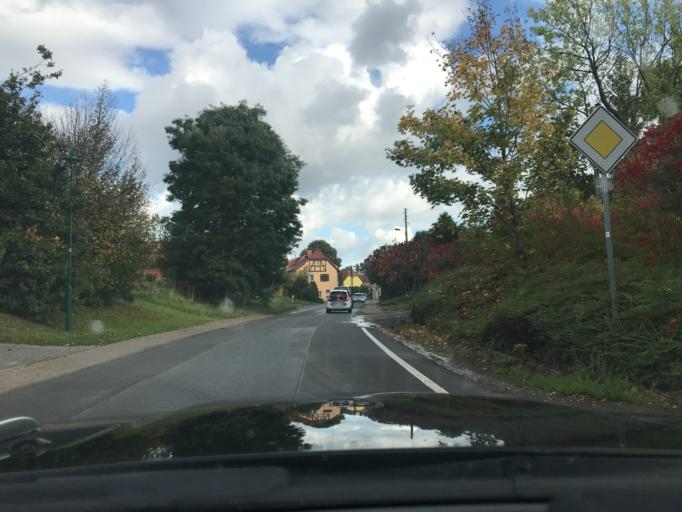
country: DE
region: Thuringia
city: Mulverstedt
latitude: 51.1187
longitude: 10.5003
